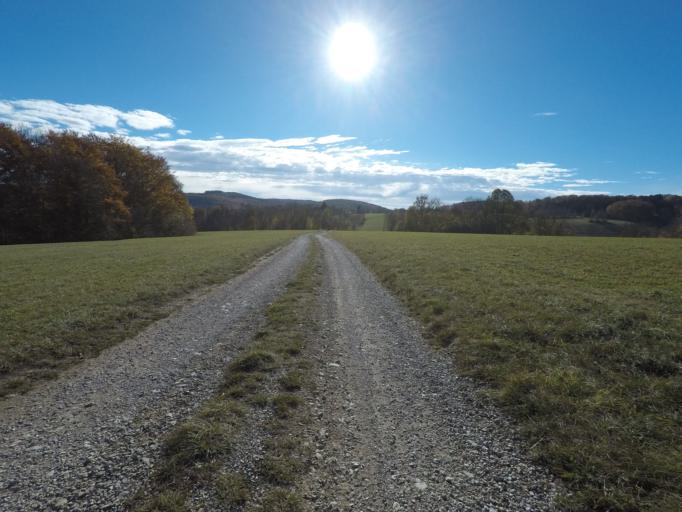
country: DE
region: Baden-Wuerttemberg
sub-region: Tuebingen Region
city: Pfullingen
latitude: 48.4141
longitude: 9.2443
